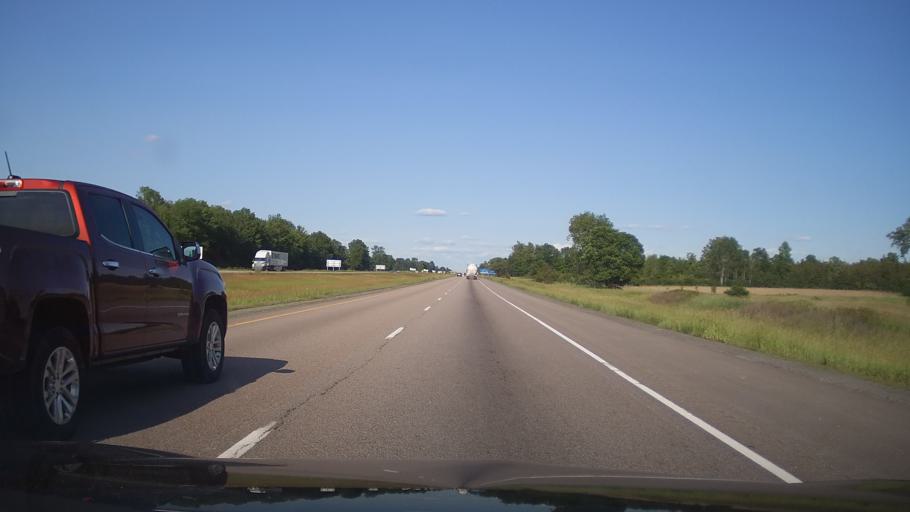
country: CA
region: Ontario
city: Deseronto
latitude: 44.2403
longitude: -77.0925
